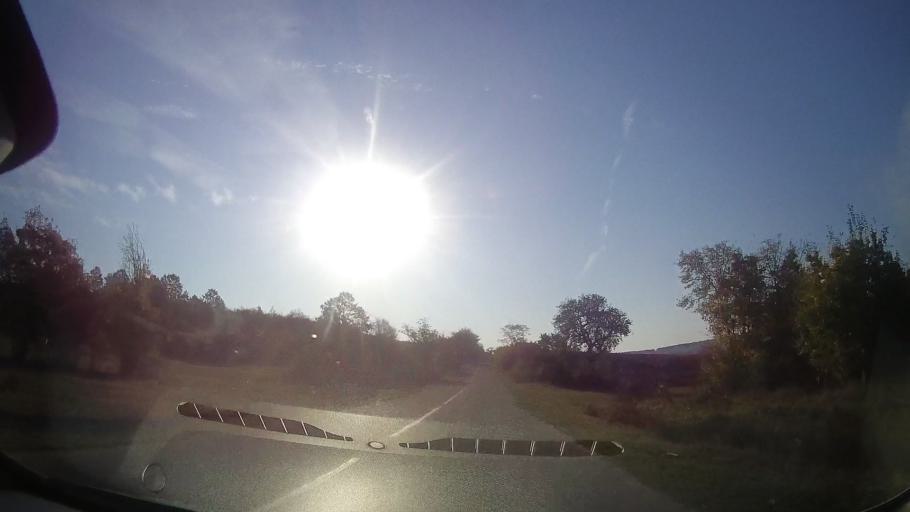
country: RO
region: Timis
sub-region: Comuna Bogda
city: Bogda
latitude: 45.9687
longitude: 21.6062
